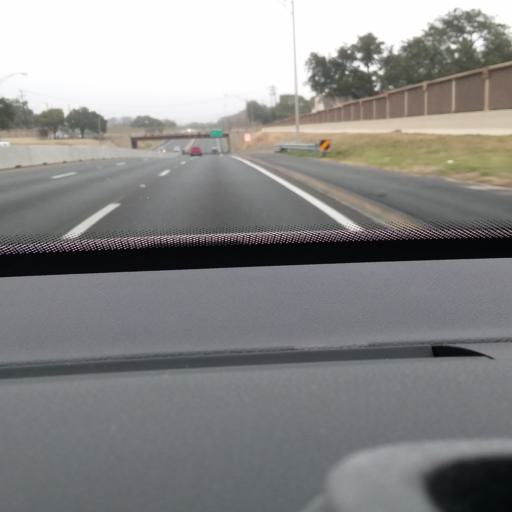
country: US
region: Texas
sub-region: Dallas County
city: Highland Park
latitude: 32.8452
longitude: -96.7864
